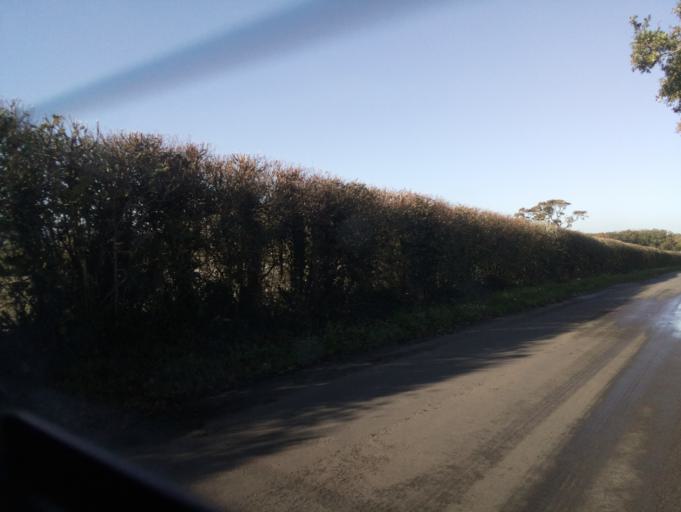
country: GB
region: England
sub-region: Dorset
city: Sherborne
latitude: 50.8626
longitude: -2.5151
